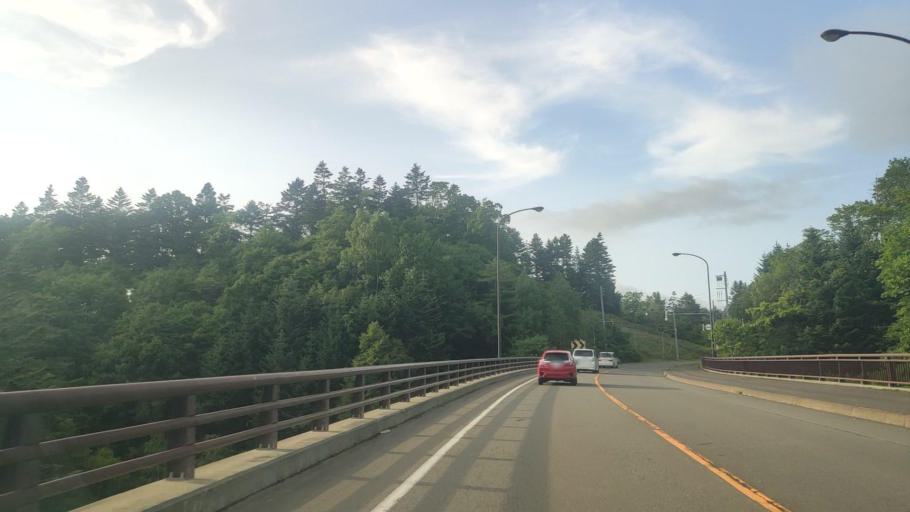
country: JP
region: Hokkaido
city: Iwamizawa
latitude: 43.0256
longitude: 141.9539
